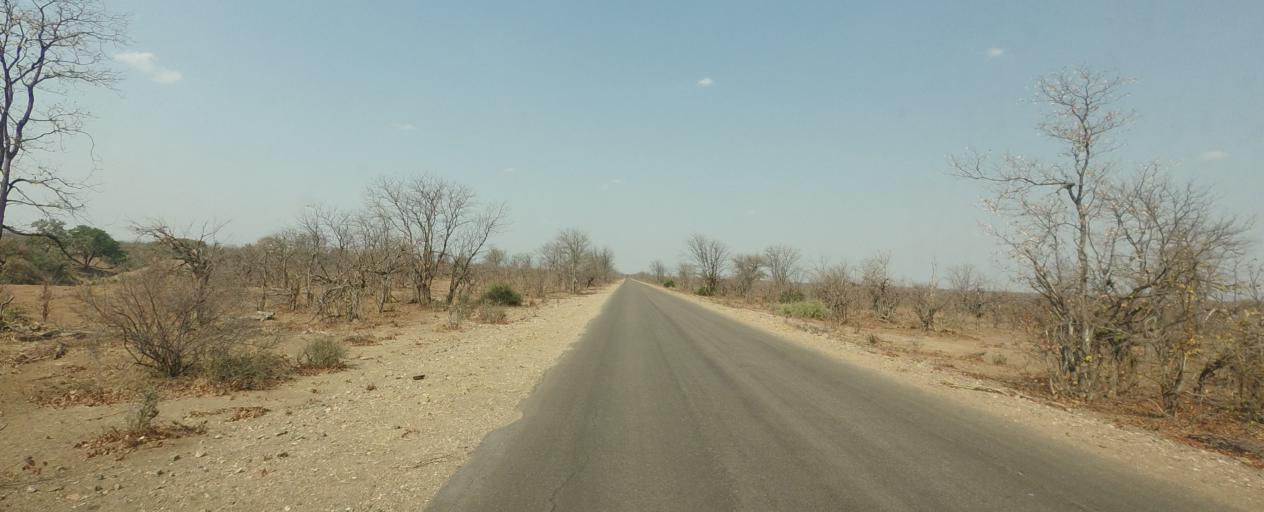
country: ZA
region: Limpopo
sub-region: Mopani District Municipality
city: Giyani
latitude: -23.1687
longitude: 31.3353
